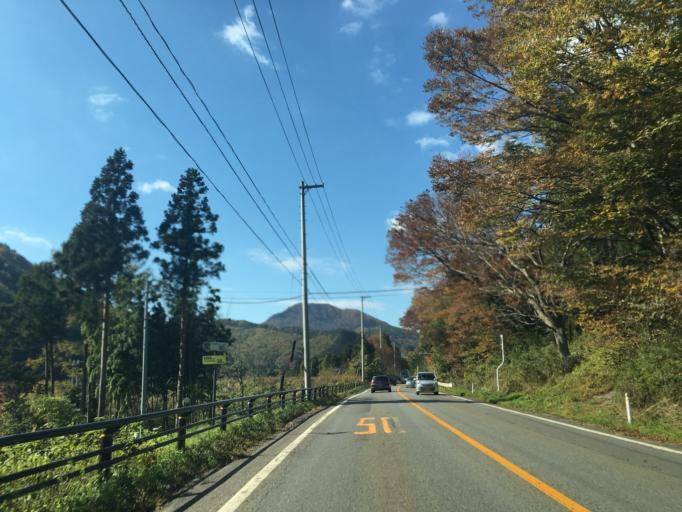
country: JP
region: Fukushima
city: Inawashiro
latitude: 37.4934
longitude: 140.2229
